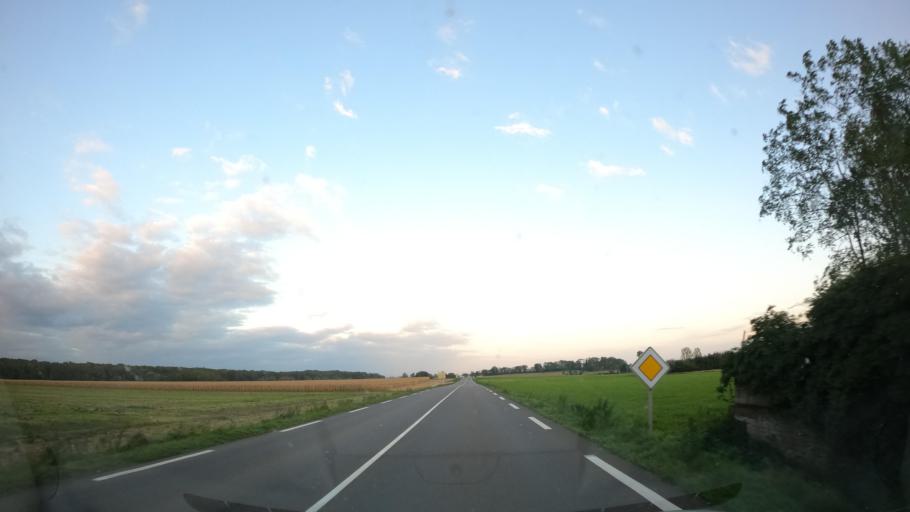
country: FR
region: Bourgogne
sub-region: Departement de Saone-et-Loire
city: Pierre-de-Bresse
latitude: 46.9602
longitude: 5.2431
